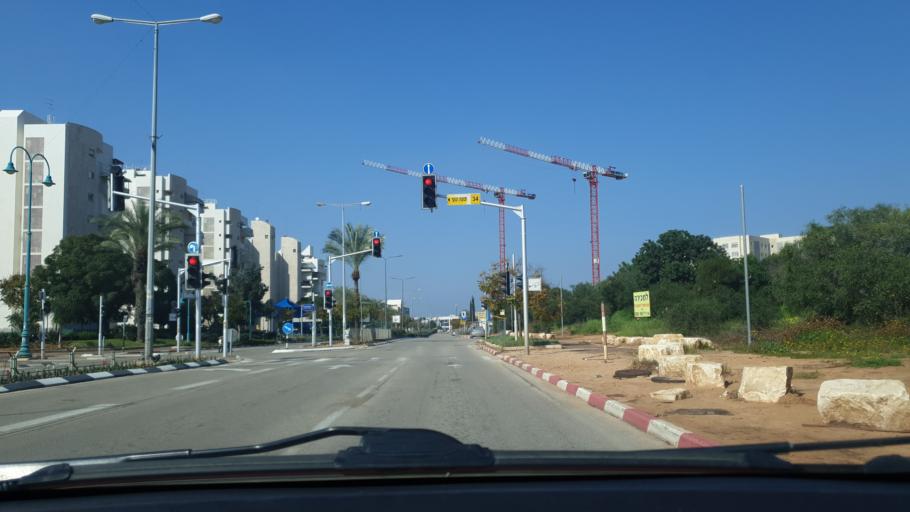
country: IL
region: Central District
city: Bet Dagan
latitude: 31.9737
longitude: 34.8178
